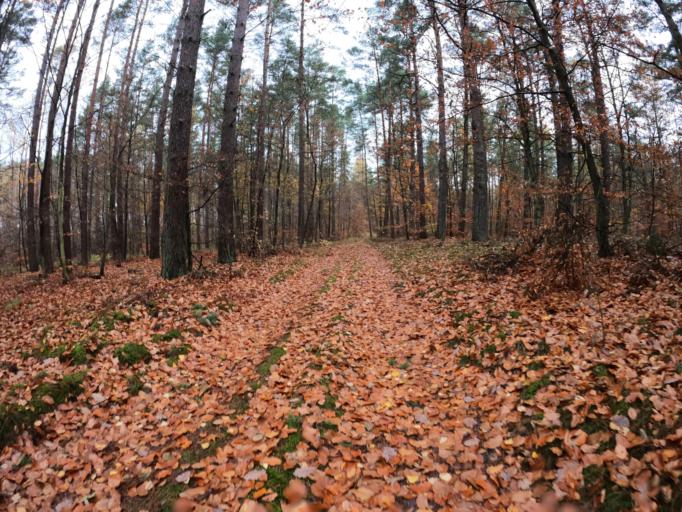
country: PL
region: West Pomeranian Voivodeship
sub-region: Powiat walecki
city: Tuczno
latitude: 53.2782
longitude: 16.2468
